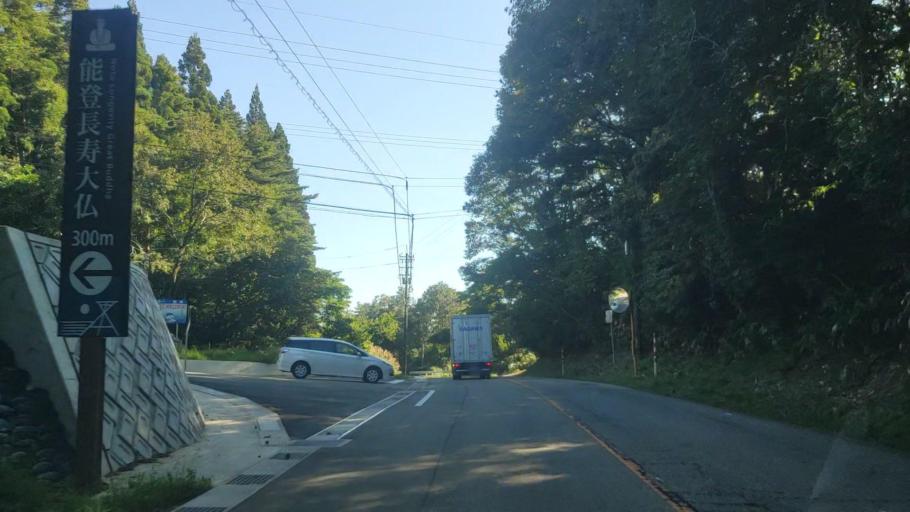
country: JP
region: Ishikawa
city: Nanao
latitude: 37.2115
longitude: 136.9080
